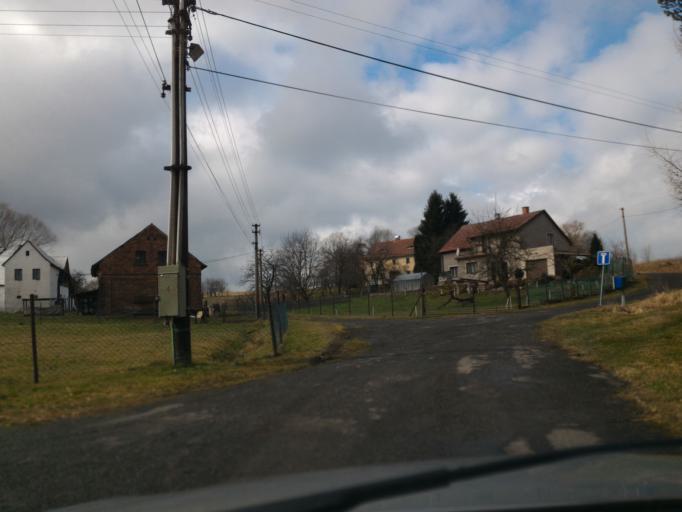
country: CZ
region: Liberecky
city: Visnova
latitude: 50.9998
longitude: 14.9863
